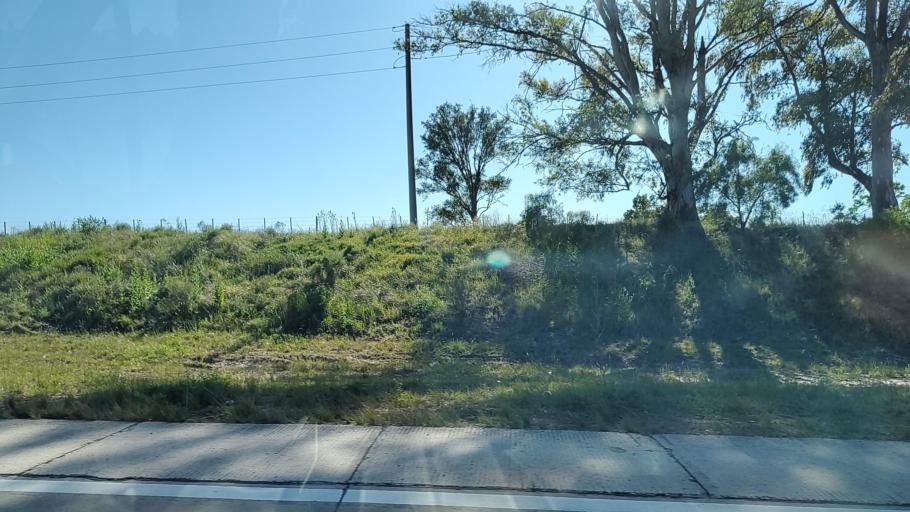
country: AR
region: Entre Rios
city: Villa Elisa
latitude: -32.0422
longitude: -58.2714
